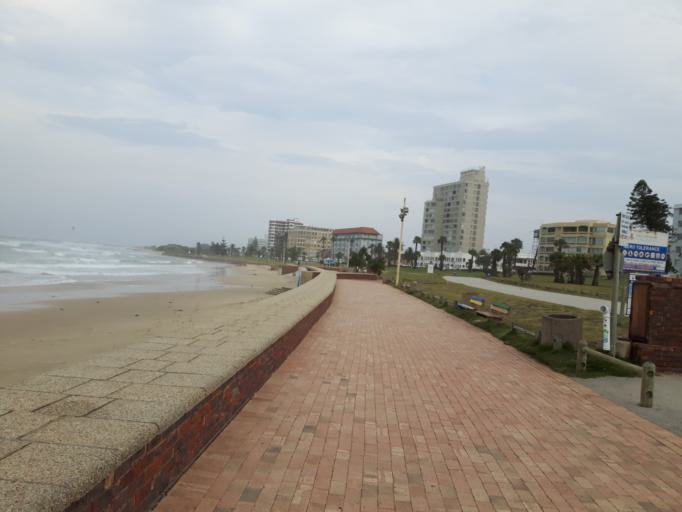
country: ZA
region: Eastern Cape
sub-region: Nelson Mandela Bay Metropolitan Municipality
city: Port Elizabeth
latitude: -33.9809
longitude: 25.6592
